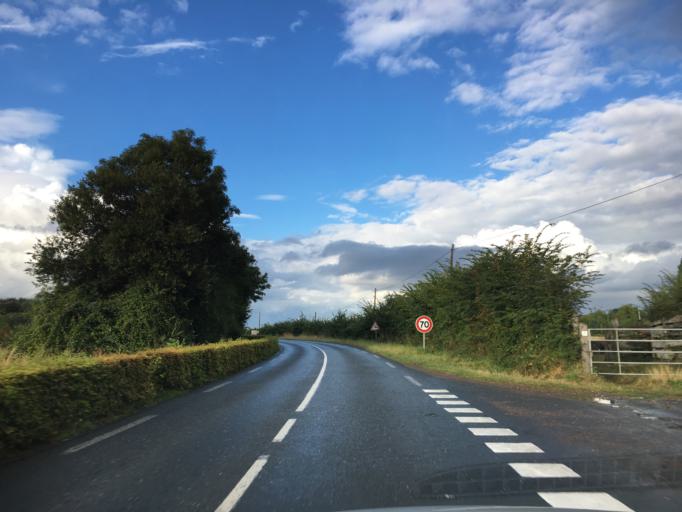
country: FR
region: Lower Normandy
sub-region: Departement du Calvados
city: Amfreville
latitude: 49.2656
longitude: -0.2231
